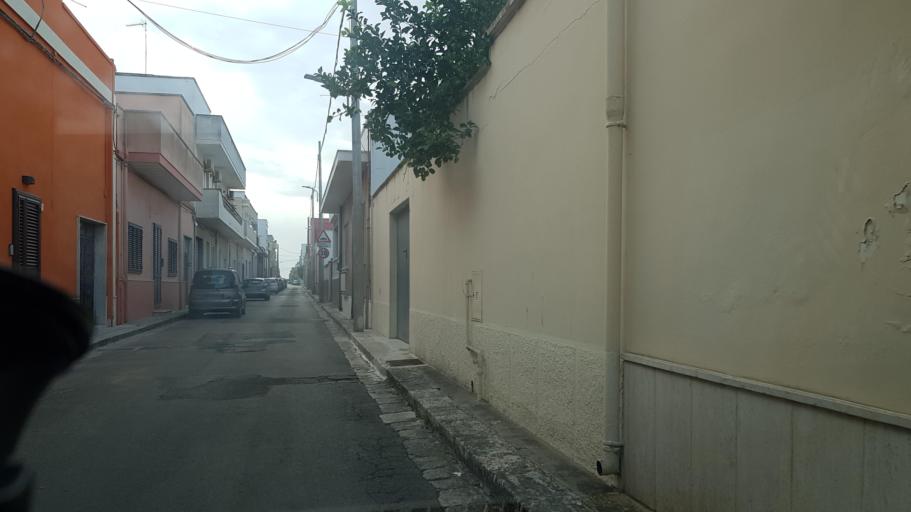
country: IT
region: Apulia
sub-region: Provincia di Lecce
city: Trepuzzi
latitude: 40.4091
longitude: 18.0701
